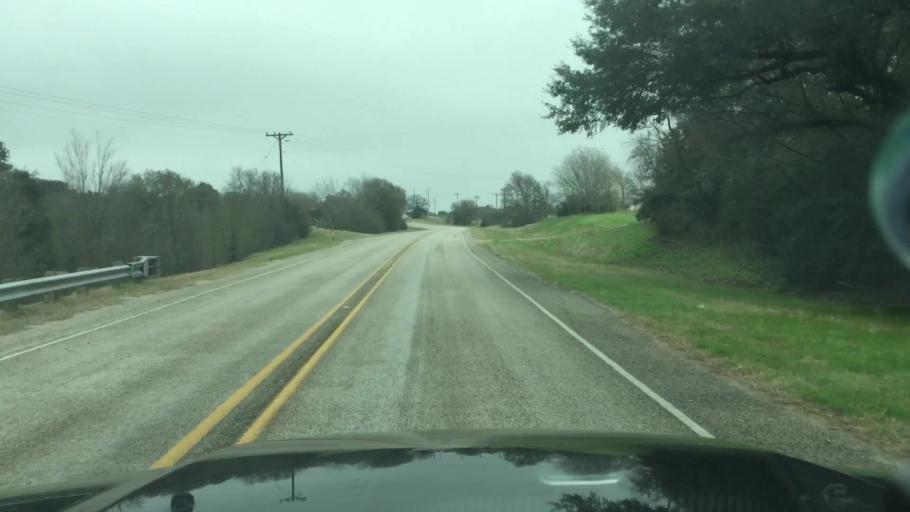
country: US
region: Texas
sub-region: Fayette County
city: La Grange
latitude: 30.0082
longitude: -96.9088
